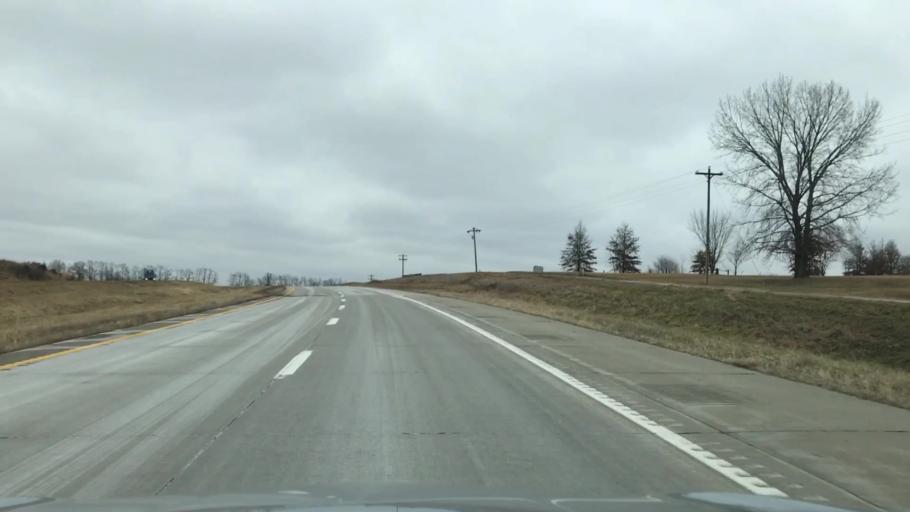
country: US
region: Missouri
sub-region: Livingston County
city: Chillicothe
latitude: 39.7379
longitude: -93.6357
